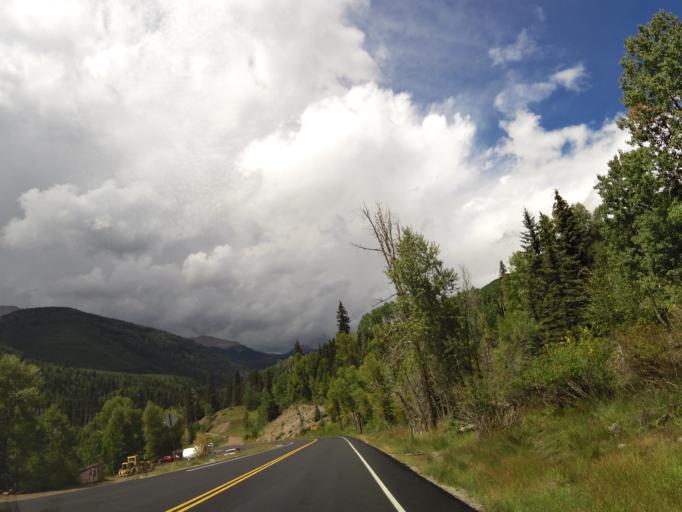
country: US
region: Colorado
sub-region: San Juan County
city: Silverton
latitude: 37.6584
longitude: -107.8091
